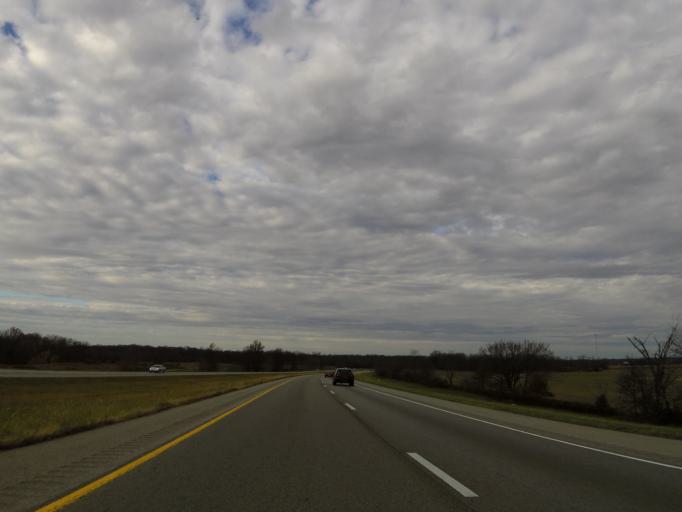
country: US
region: Illinois
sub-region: Clinton County
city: Wamac
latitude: 38.3623
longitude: -89.0753
